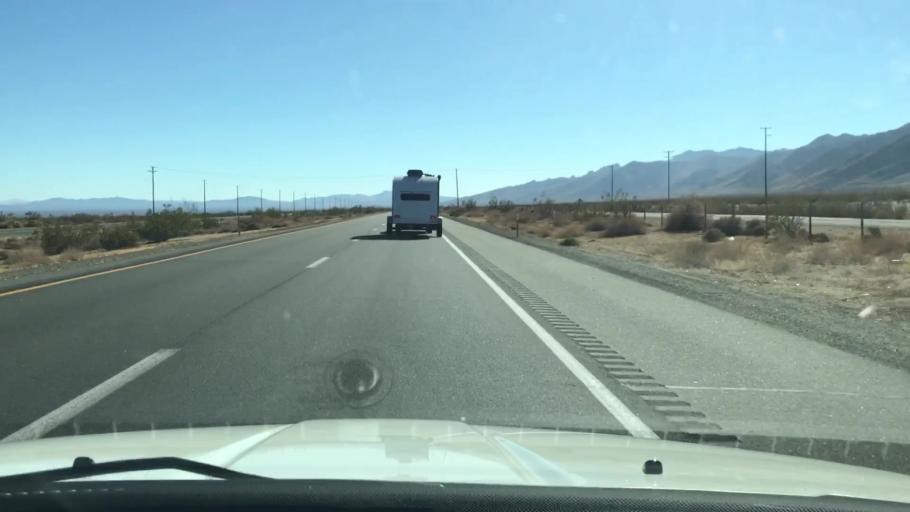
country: US
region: California
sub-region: Kern County
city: Inyokern
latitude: 35.8381
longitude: -117.8750
